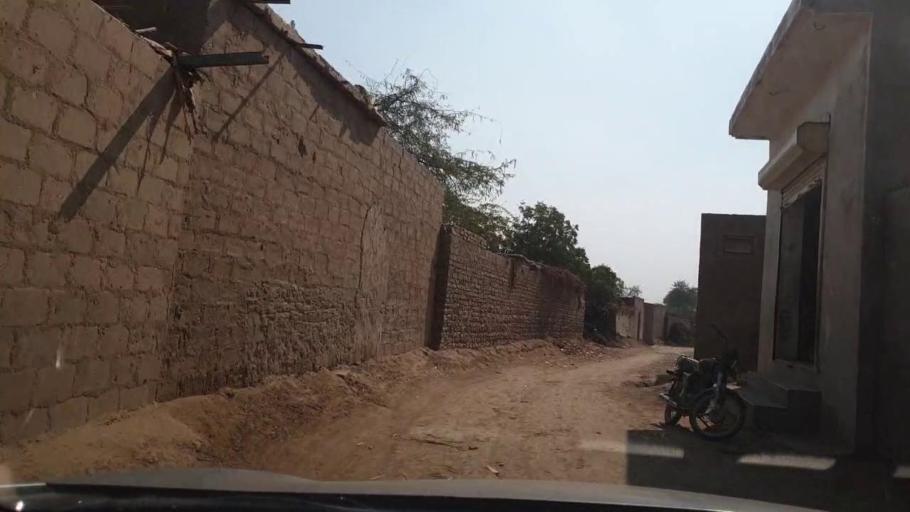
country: PK
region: Sindh
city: Tando Allahyar
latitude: 25.5050
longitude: 68.7921
